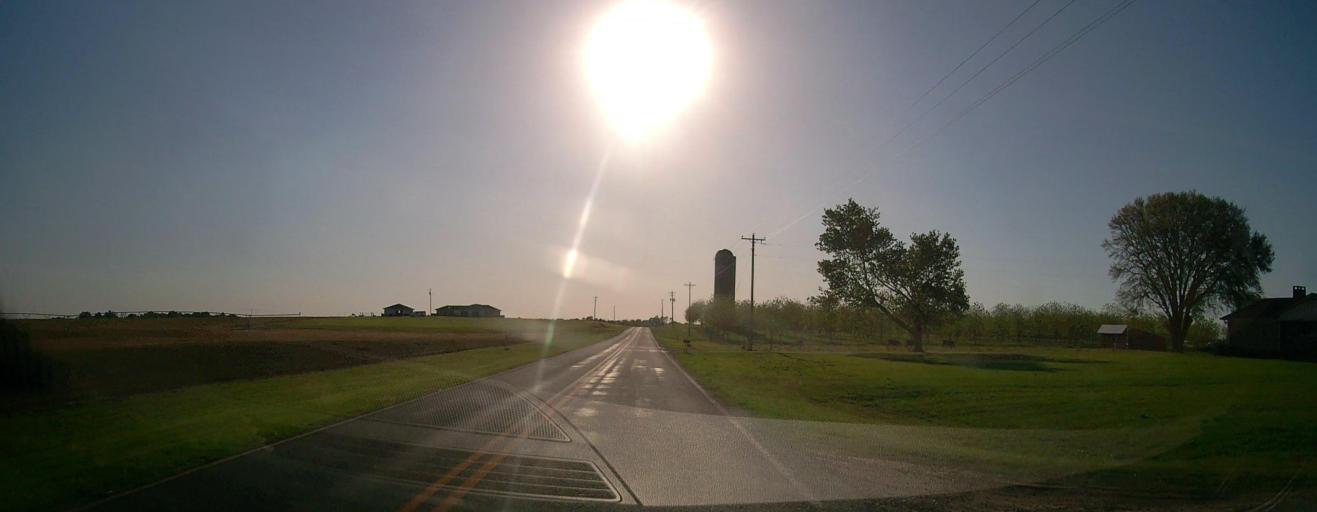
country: US
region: Georgia
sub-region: Macon County
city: Montezuma
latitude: 32.3179
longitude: -83.9785
